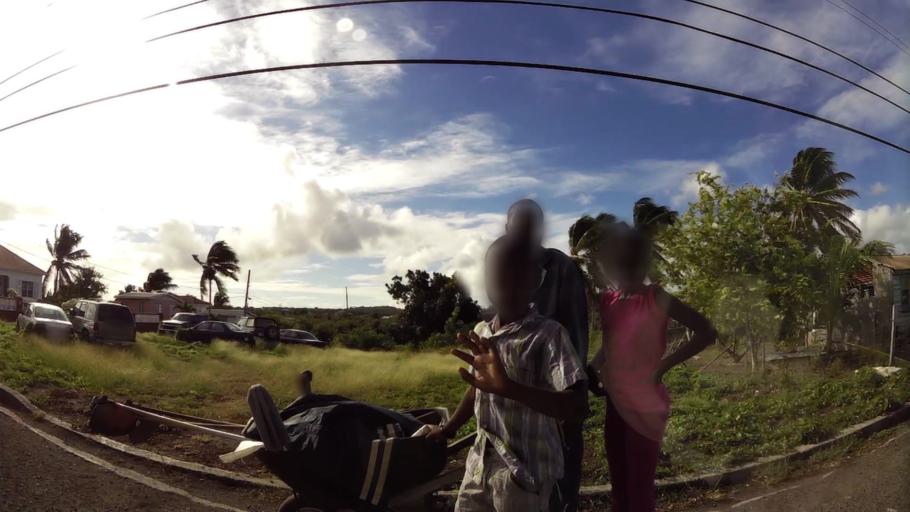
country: AG
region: Saint Peter
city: Parham
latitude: 17.0943
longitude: -61.7249
